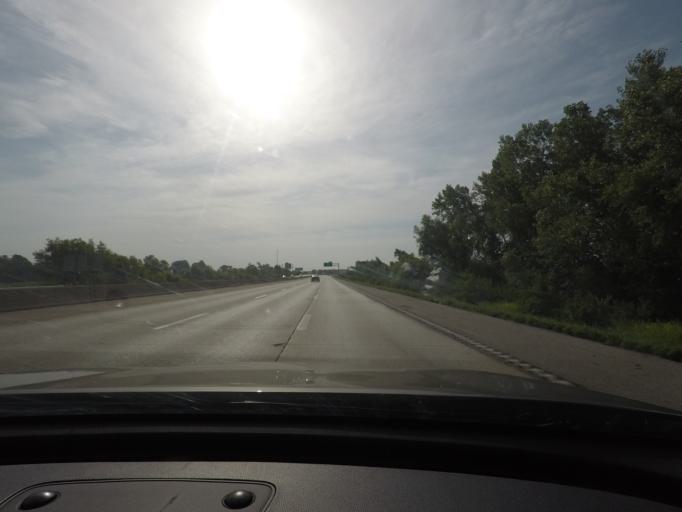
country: US
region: Missouri
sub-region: Saint Louis County
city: Bridgeton
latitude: 38.7902
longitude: -90.4314
